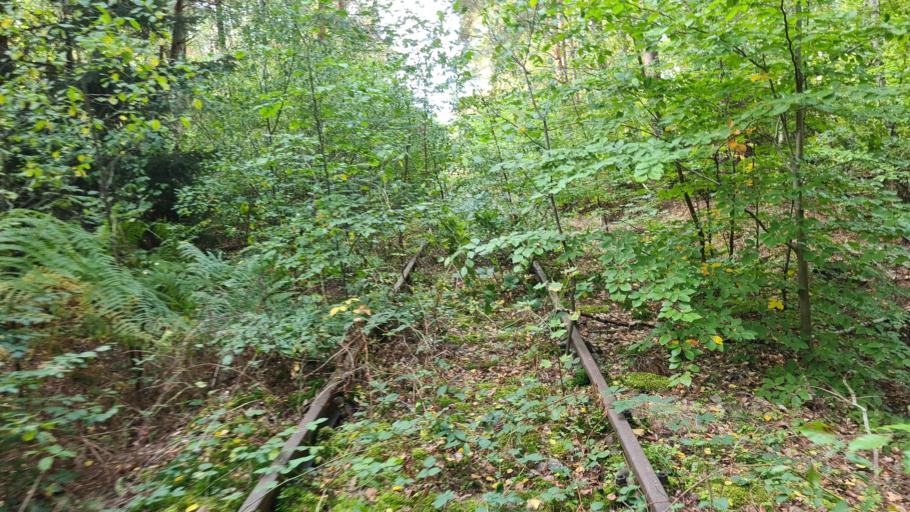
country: DE
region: Brandenburg
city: Doberlug-Kirchhain
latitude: 51.6281
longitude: 13.5242
